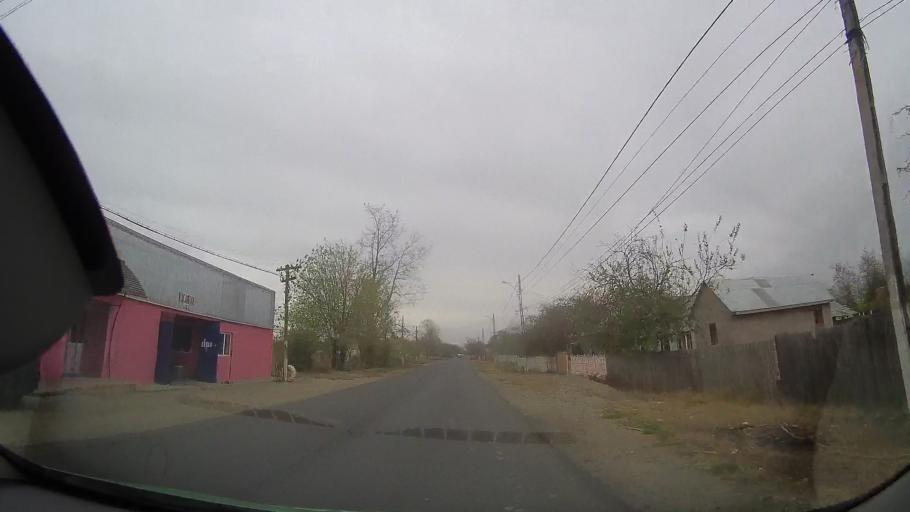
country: RO
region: Braila
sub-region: Comuna Ulmu
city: Ulmu
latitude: 44.9509
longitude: 27.3186
